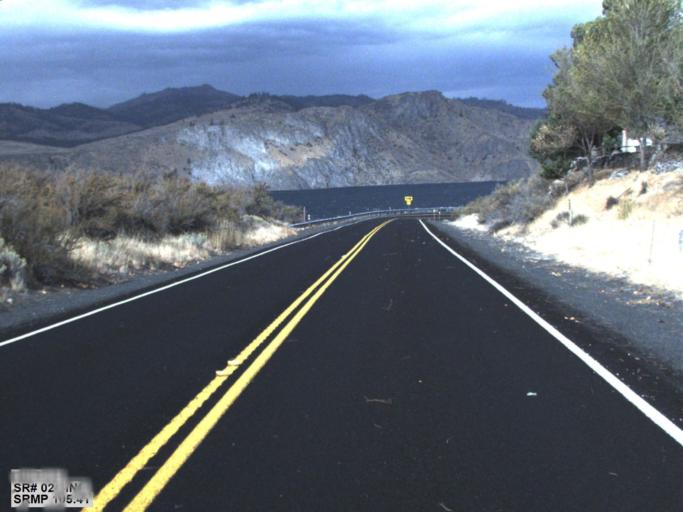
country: US
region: Washington
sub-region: Okanogan County
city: Coulee Dam
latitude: 47.9144
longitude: -118.6971
